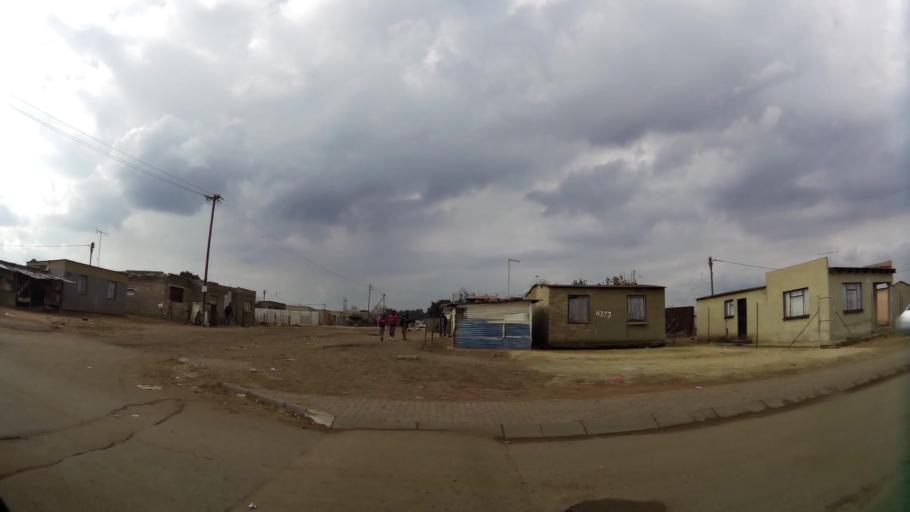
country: ZA
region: Gauteng
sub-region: Sedibeng District Municipality
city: Vanderbijlpark
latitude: -26.6992
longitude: 27.8019
